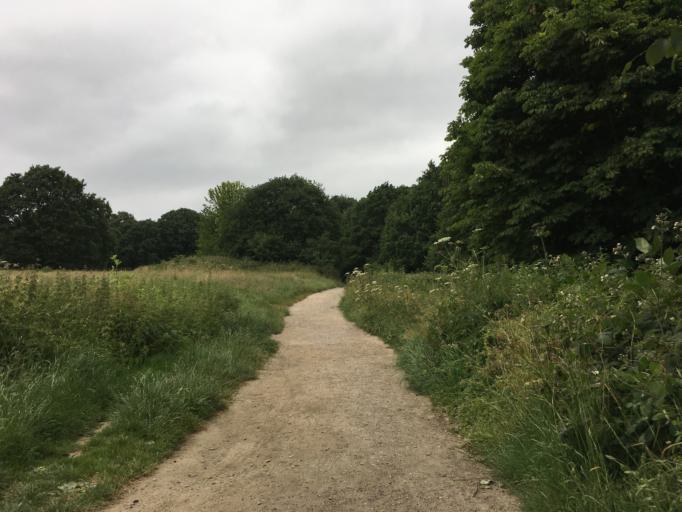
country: GB
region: England
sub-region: Greater London
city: Belsize Park
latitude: 51.5600
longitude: -0.1670
